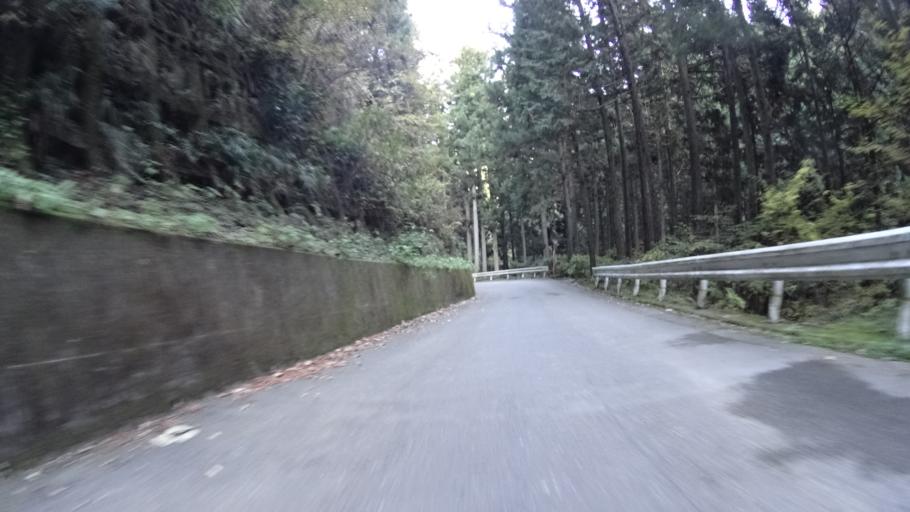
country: JP
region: Yamanashi
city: Uenohara
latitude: 35.6589
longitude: 139.1763
